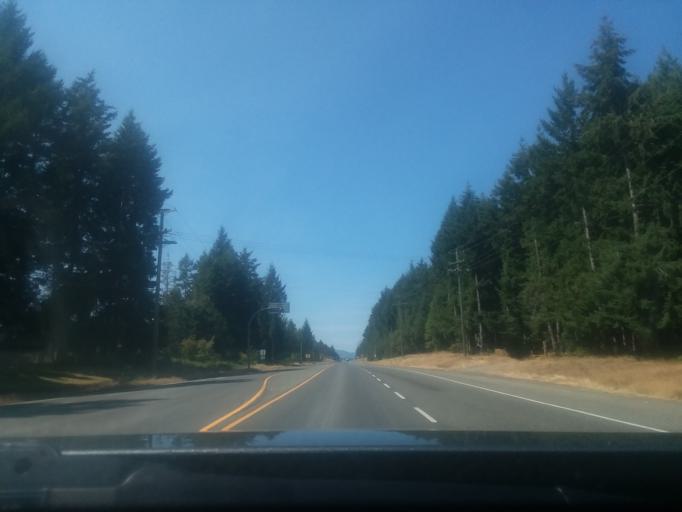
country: CA
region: British Columbia
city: Courtenay
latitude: 49.7151
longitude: -124.9346
